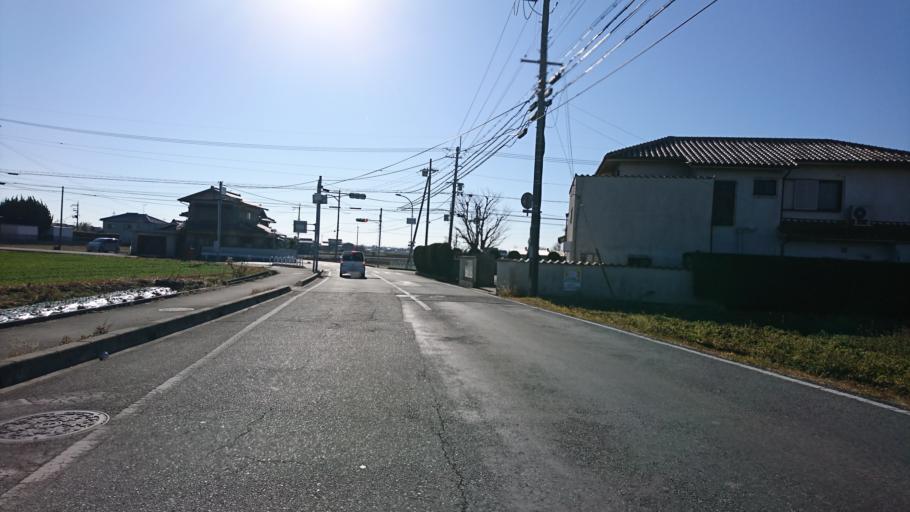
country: JP
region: Hyogo
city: Miki
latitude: 34.7378
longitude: 134.9441
